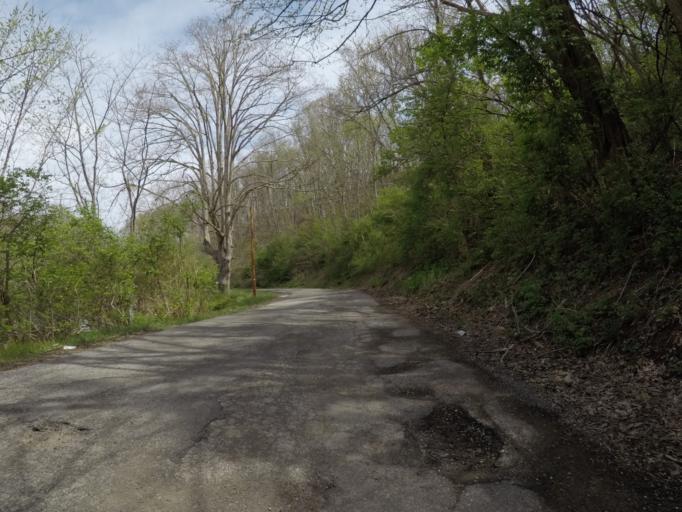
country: US
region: West Virginia
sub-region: Wayne County
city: Lavalette
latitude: 38.3444
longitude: -82.3813
